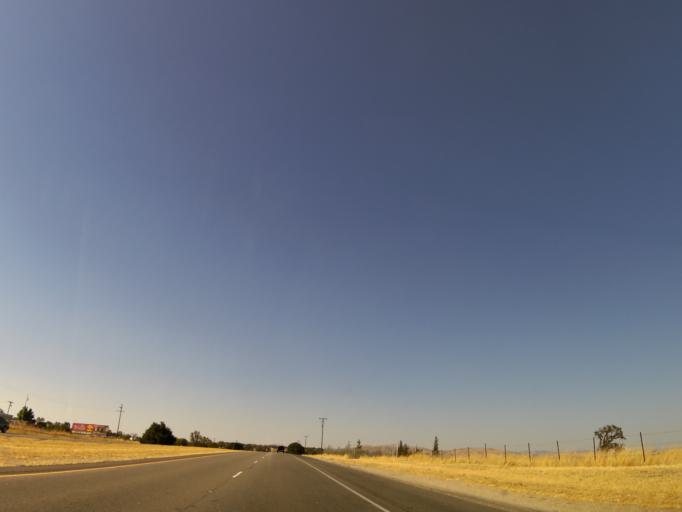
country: US
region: California
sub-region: San Luis Obispo County
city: Paso Robles
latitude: 35.6870
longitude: -120.6967
